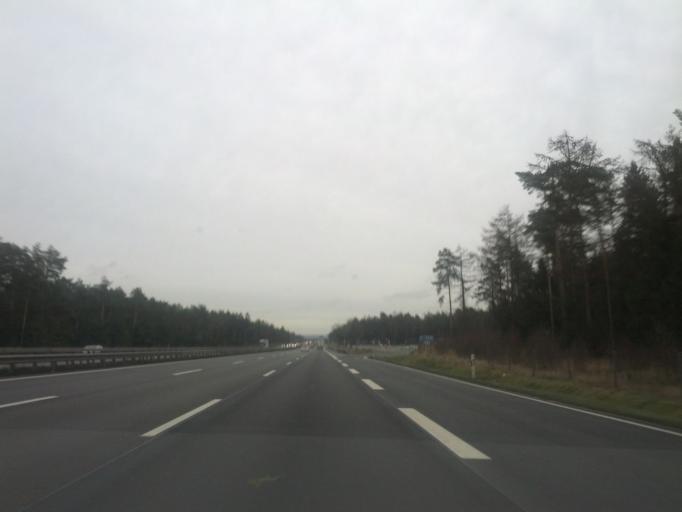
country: DE
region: Lower Saxony
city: Heidenau
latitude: 53.3423
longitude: 9.6515
